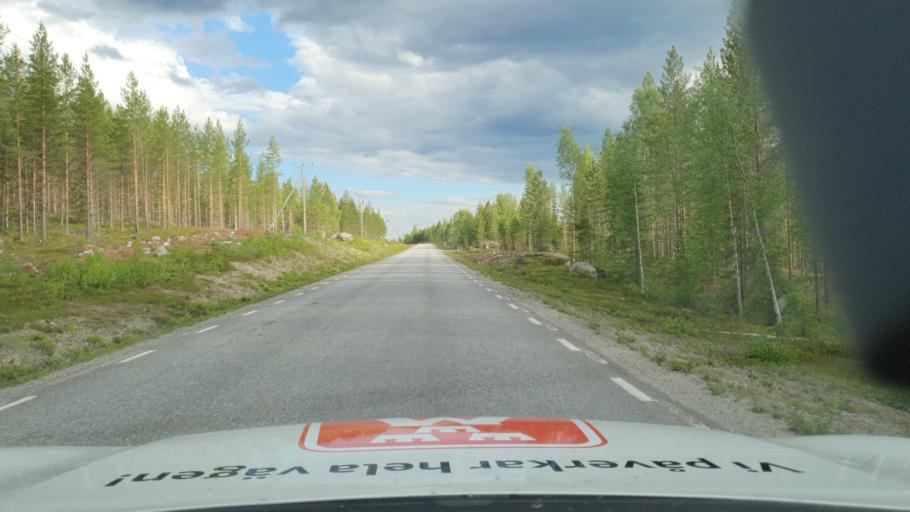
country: SE
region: Vaesterbotten
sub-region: Vindelns Kommun
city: Vindeln
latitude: 64.4037
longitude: 19.6590
